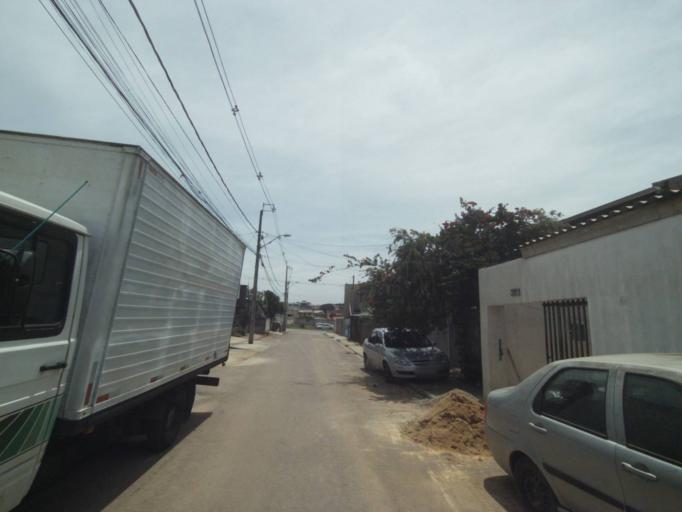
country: BR
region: Parana
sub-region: Curitiba
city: Curitiba
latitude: -25.4984
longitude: -49.3402
